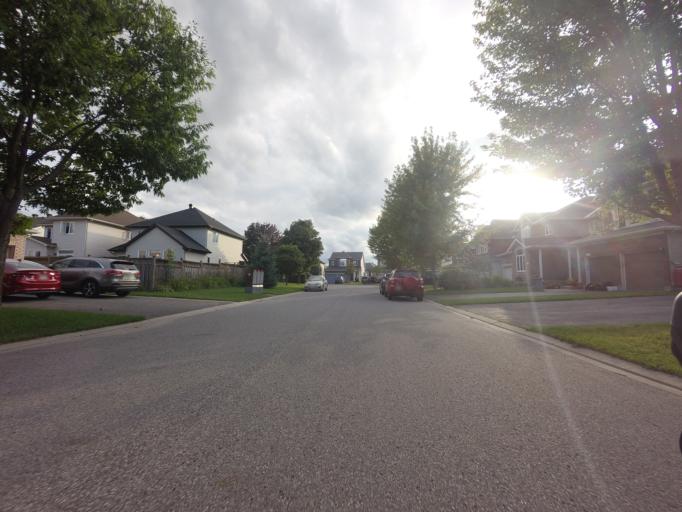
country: CA
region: Ontario
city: Bells Corners
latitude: 45.2888
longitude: -75.7135
